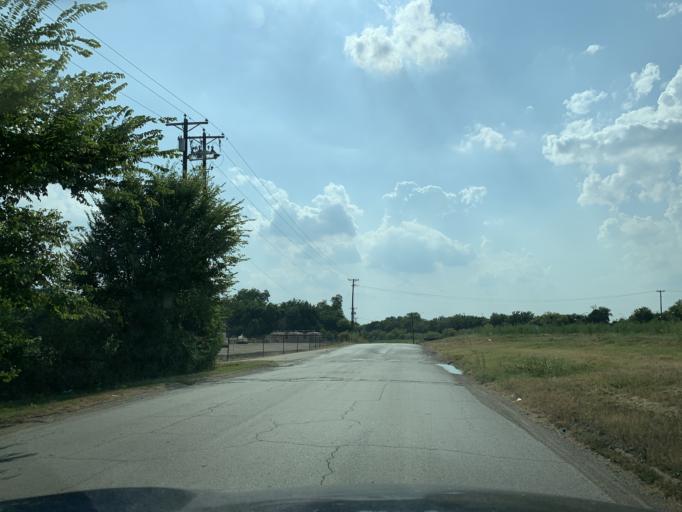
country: US
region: Texas
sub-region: Tarrant County
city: Richland Hills
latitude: 32.7946
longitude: -97.2315
